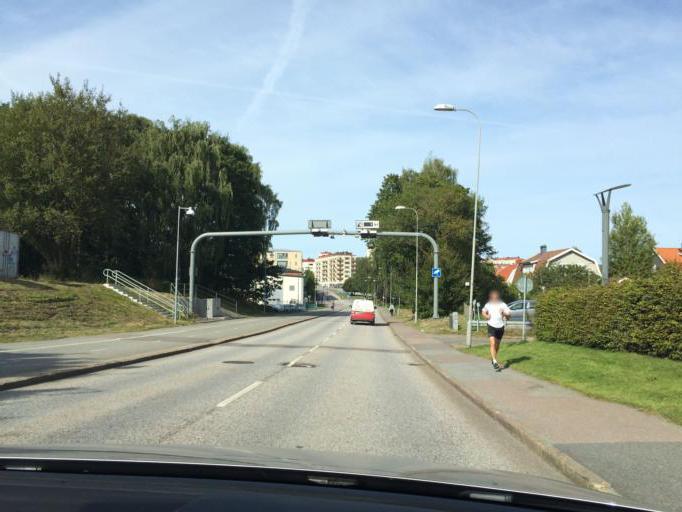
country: SE
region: Vaestra Goetaland
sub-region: Goteborg
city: Goeteborg
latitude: 57.6825
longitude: 11.9846
